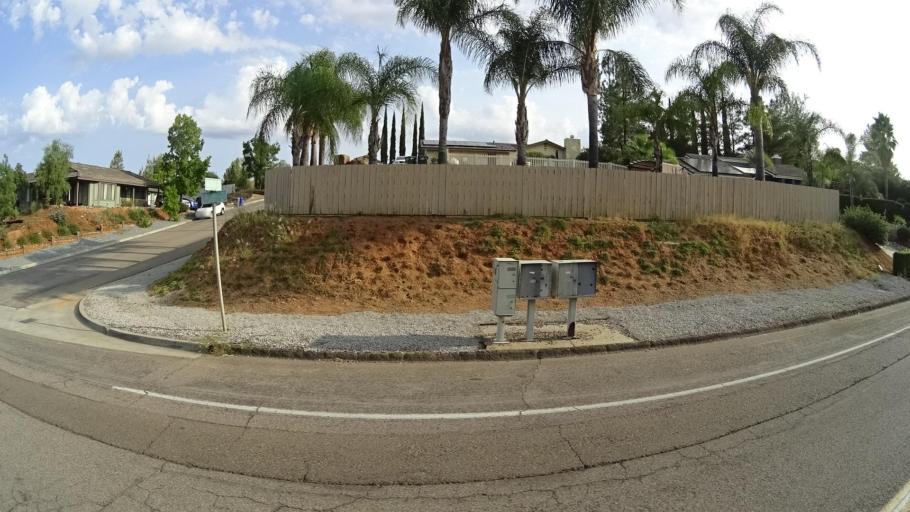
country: US
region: California
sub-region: San Diego County
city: San Diego Country Estates
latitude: 33.0089
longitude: -116.7971
